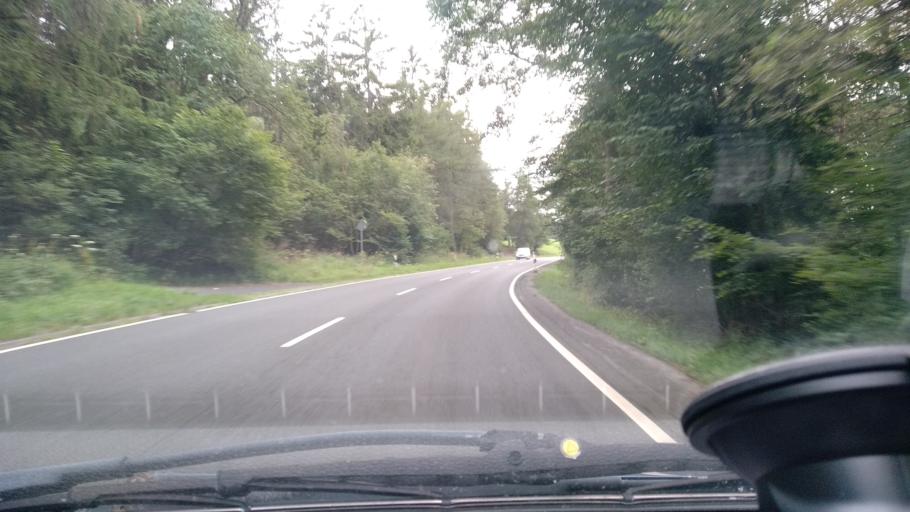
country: DE
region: Hesse
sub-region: Regierungsbezirk Giessen
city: Haiger
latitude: 50.8511
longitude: 8.2172
